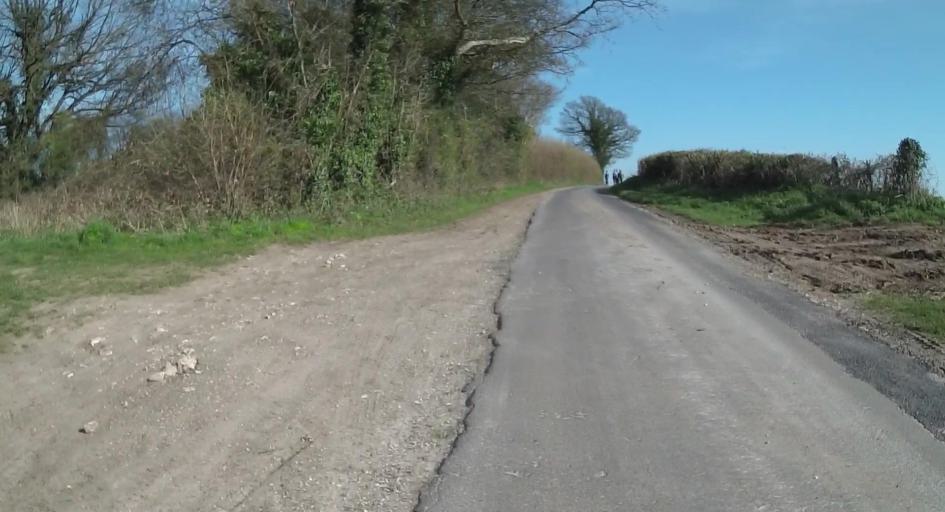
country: GB
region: England
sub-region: Hampshire
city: Highclere
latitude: 51.2639
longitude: -1.3892
